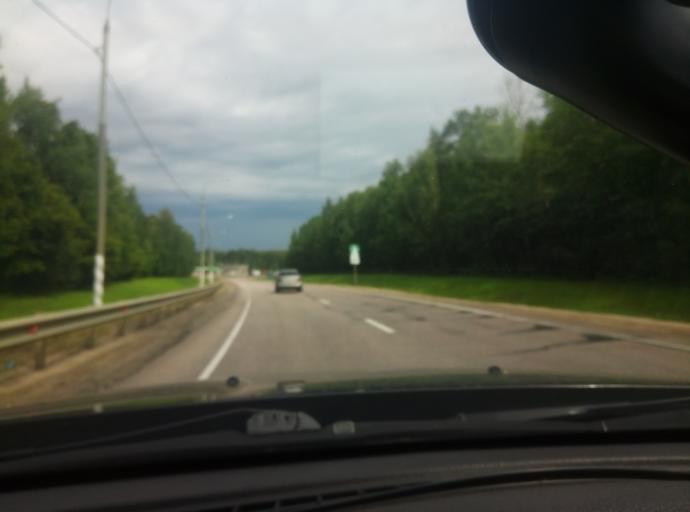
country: RU
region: Tula
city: Leninskiy
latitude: 54.4106
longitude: 37.5018
